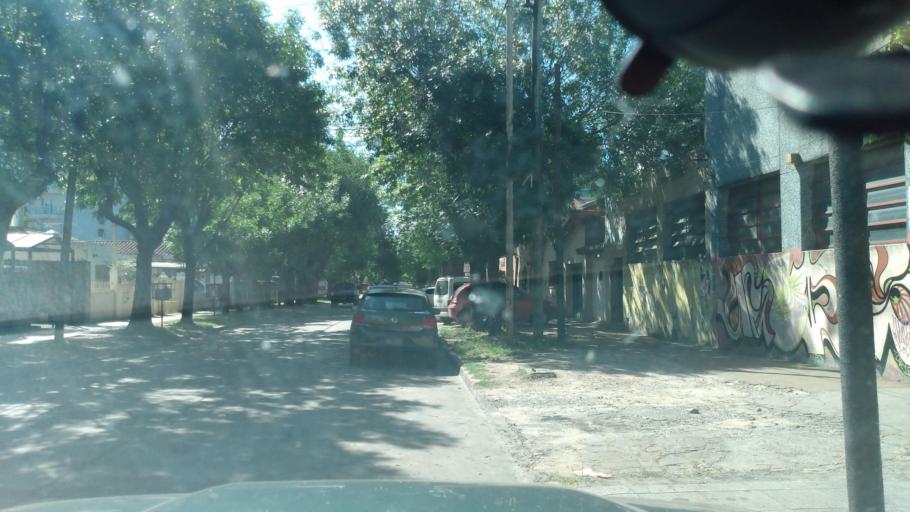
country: AR
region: Buenos Aires
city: Hurlingham
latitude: -34.5437
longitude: -58.7042
